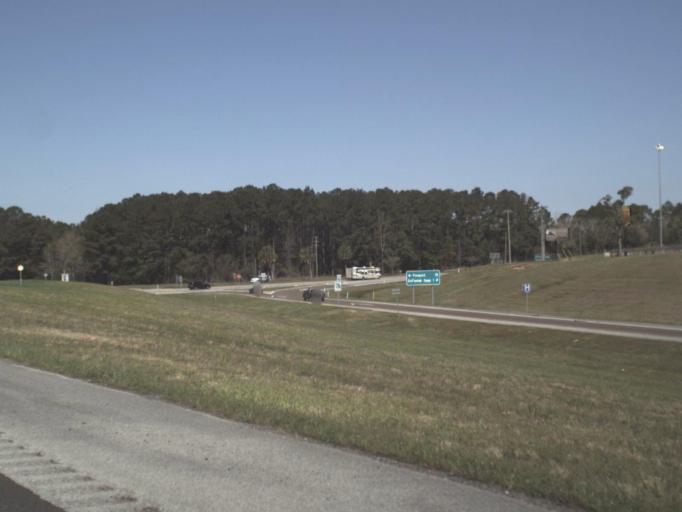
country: US
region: Florida
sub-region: Walton County
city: DeFuniak Springs
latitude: 30.6921
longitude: -86.1206
